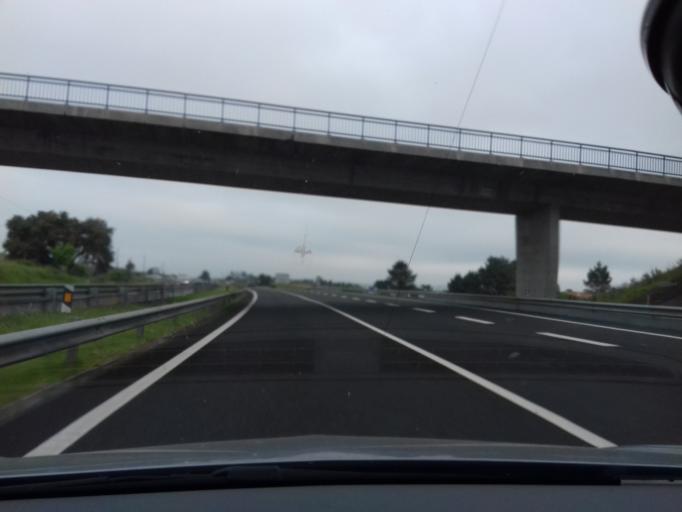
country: PT
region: Leiria
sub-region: Bombarral
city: Bombarral
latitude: 39.2544
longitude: -9.1647
